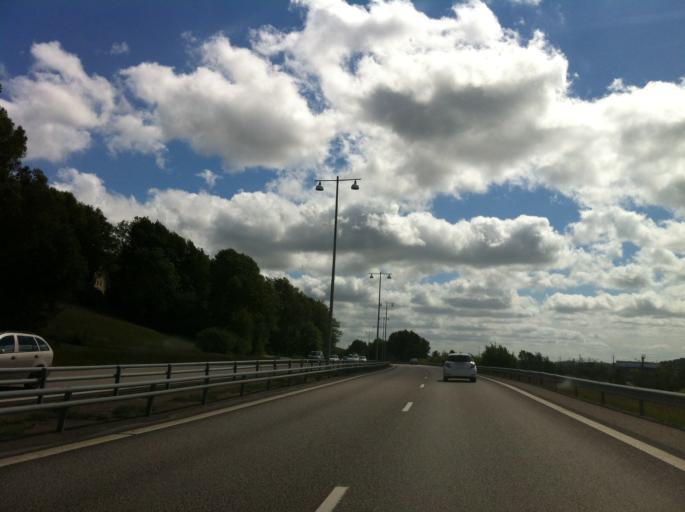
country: SE
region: Vaestra Goetaland
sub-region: Ale Kommun
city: Surte
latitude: 57.8179
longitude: 12.0151
